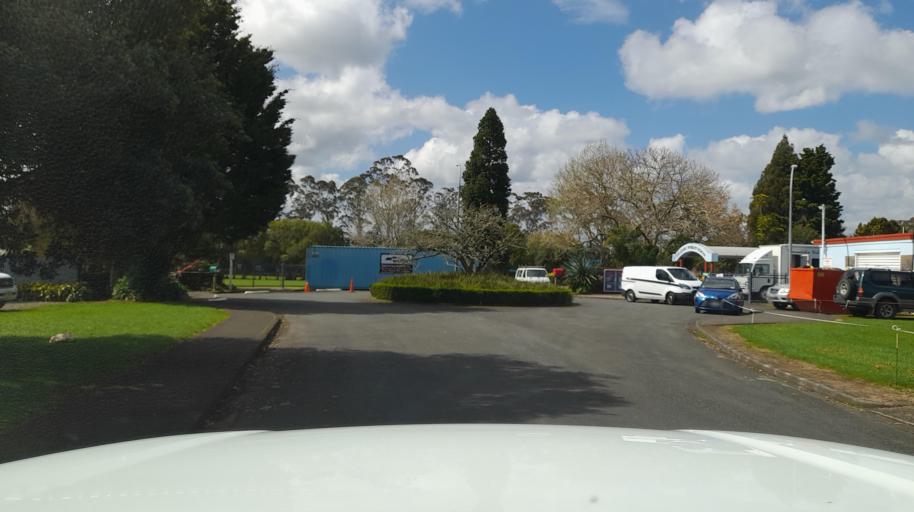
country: NZ
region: Northland
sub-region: Far North District
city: Waimate North
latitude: -35.3529
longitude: 173.8833
